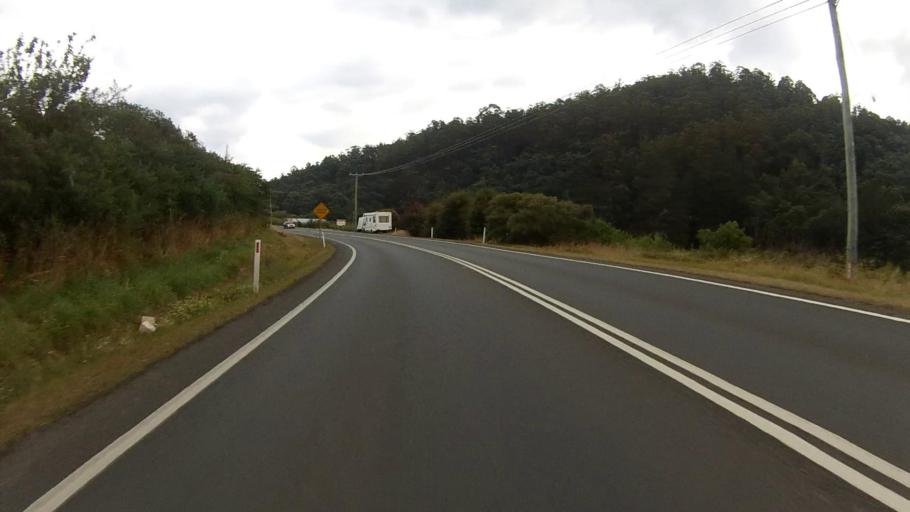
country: AU
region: Tasmania
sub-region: Huon Valley
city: Cygnet
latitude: -43.1417
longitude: 147.0637
